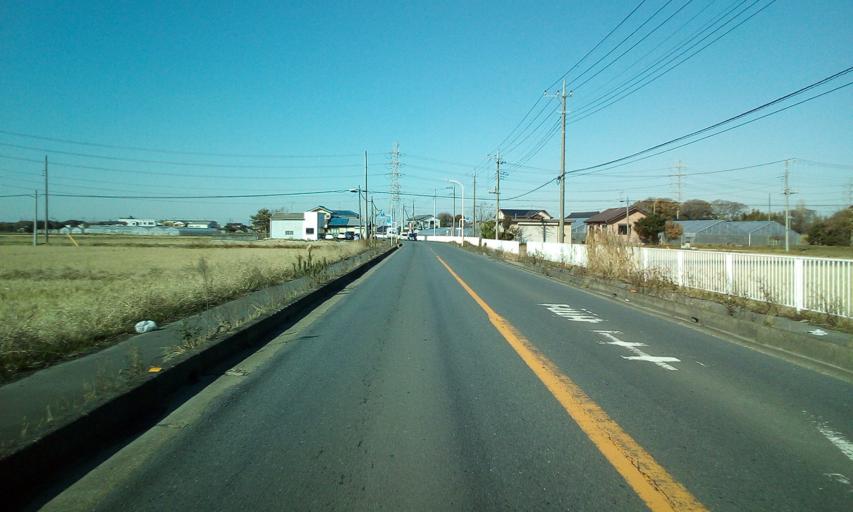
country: JP
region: Saitama
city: Yoshikawa
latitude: 35.8967
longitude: 139.8737
